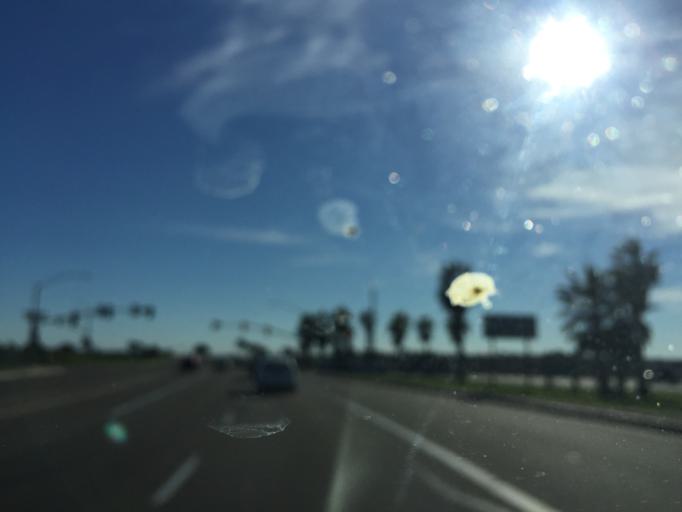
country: US
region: California
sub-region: San Diego County
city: San Diego
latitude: 32.7681
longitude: -117.2087
